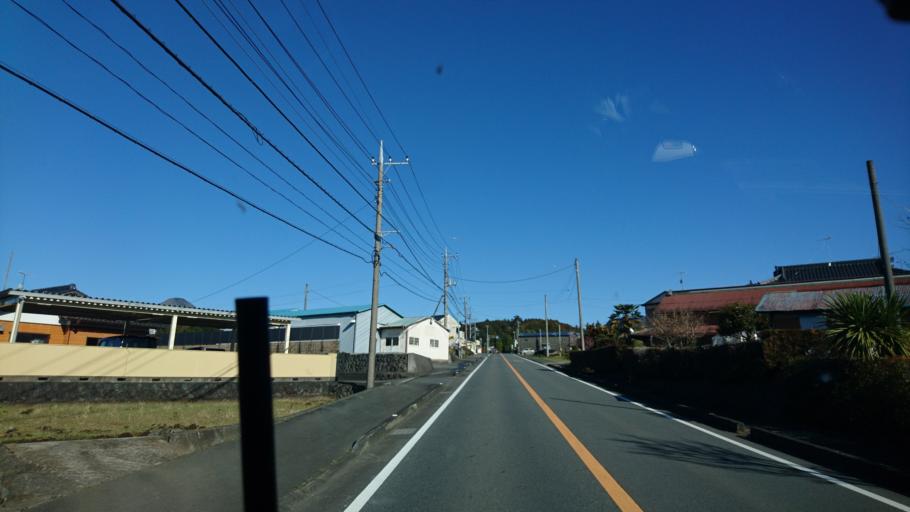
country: JP
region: Shizuoka
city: Fujinomiya
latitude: 35.2879
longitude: 138.6026
